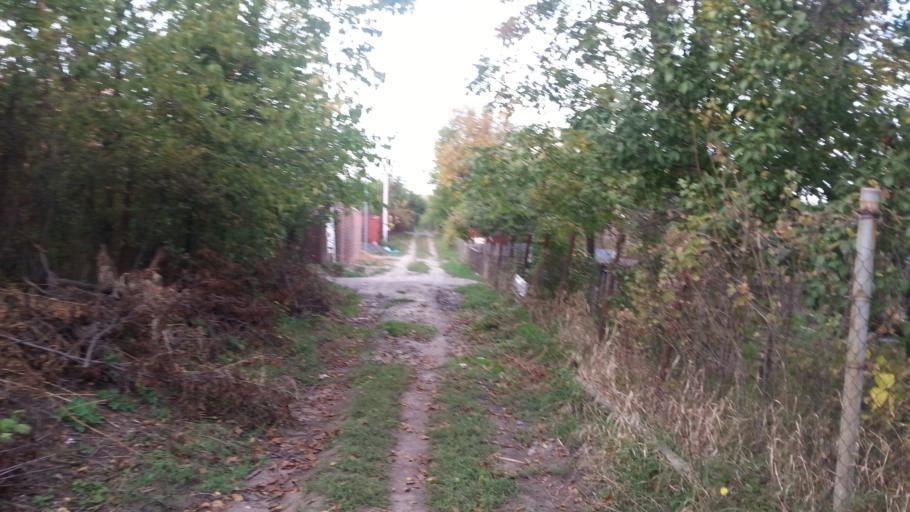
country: RU
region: Rostov
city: Severnyy
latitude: 47.2910
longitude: 39.6733
